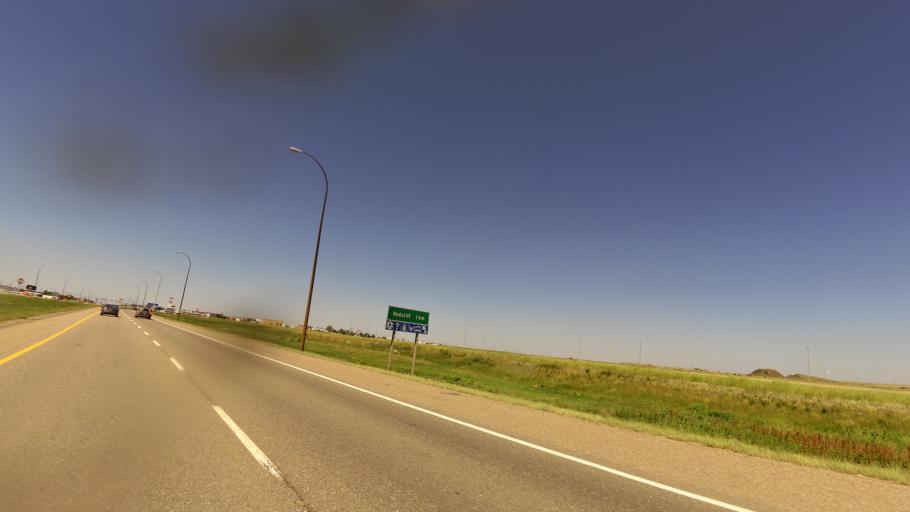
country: CA
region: Alberta
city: Medicine Hat
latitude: 50.0673
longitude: -110.7472
